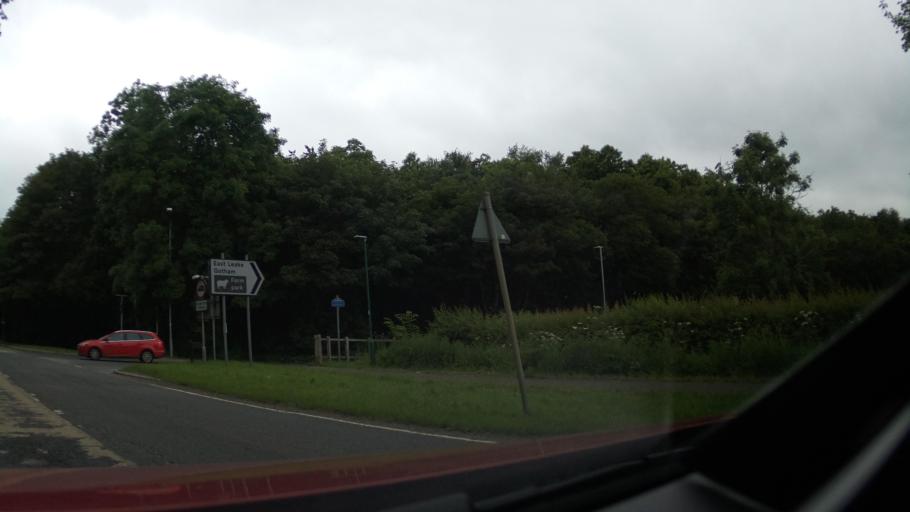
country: GB
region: England
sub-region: Nottinghamshire
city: East Leake
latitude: 52.8142
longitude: -1.1792
